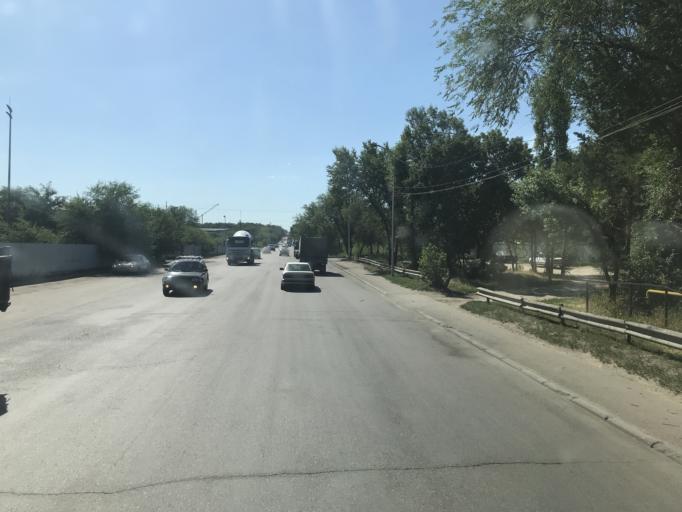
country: KZ
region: Almaty Oblysy
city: Pervomayskiy
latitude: 43.3544
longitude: 76.9174
